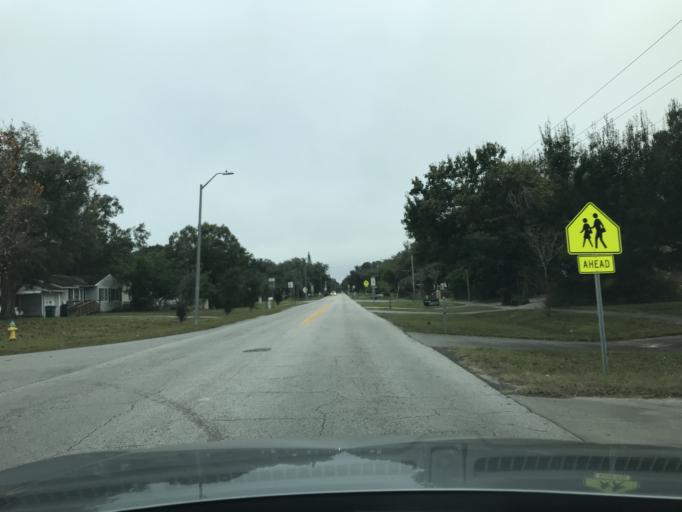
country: US
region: Florida
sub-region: Hillsborough County
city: Egypt Lake-Leto
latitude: 27.9947
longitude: -82.4762
